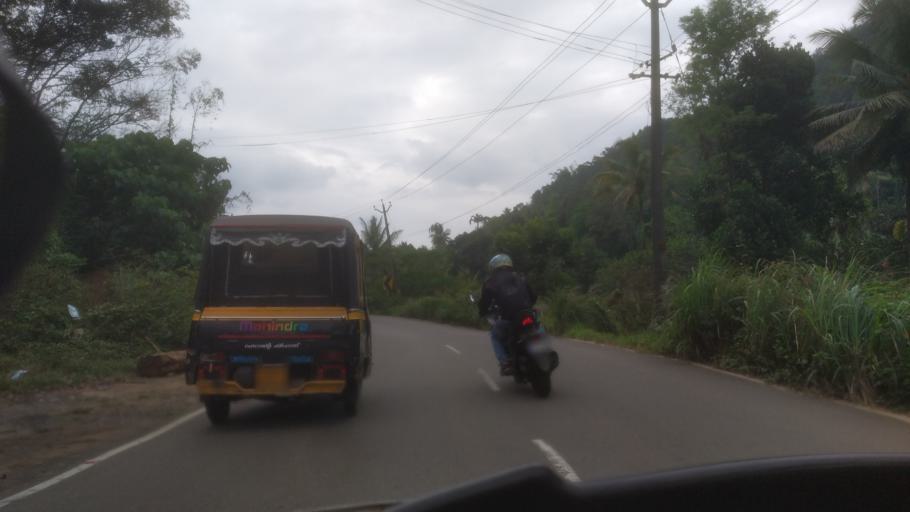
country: IN
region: Kerala
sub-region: Idukki
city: Munnar
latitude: 9.9851
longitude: 76.9871
